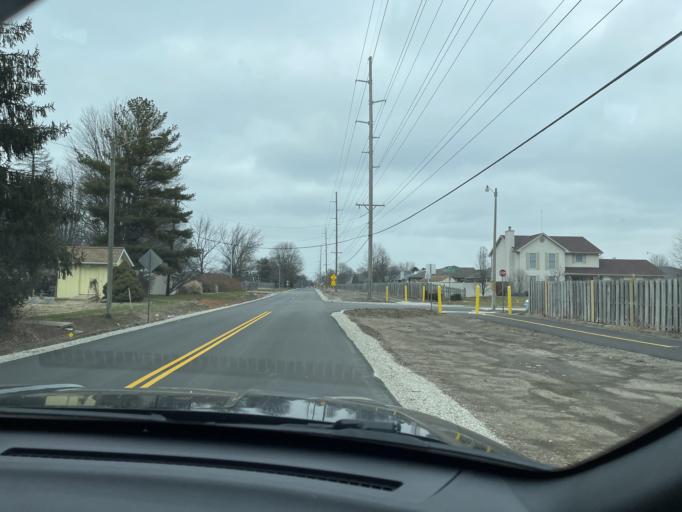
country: US
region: Illinois
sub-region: Sangamon County
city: Rochester
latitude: 39.7628
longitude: -89.5787
